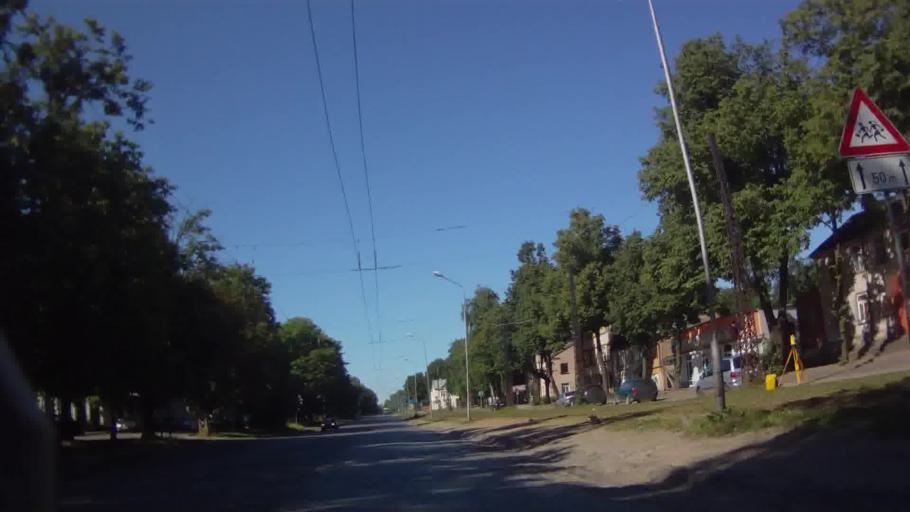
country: LV
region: Riga
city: Riga
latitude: 56.9215
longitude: 24.0889
